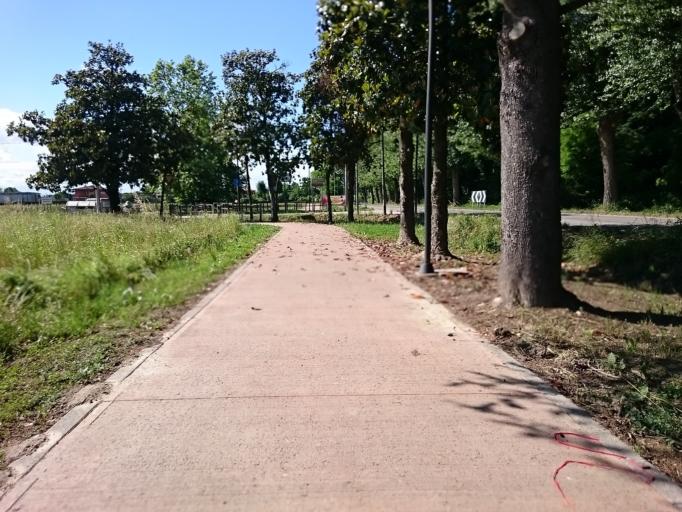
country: IT
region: Veneto
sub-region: Provincia di Padova
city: Saonara
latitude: 45.3616
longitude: 11.9891
